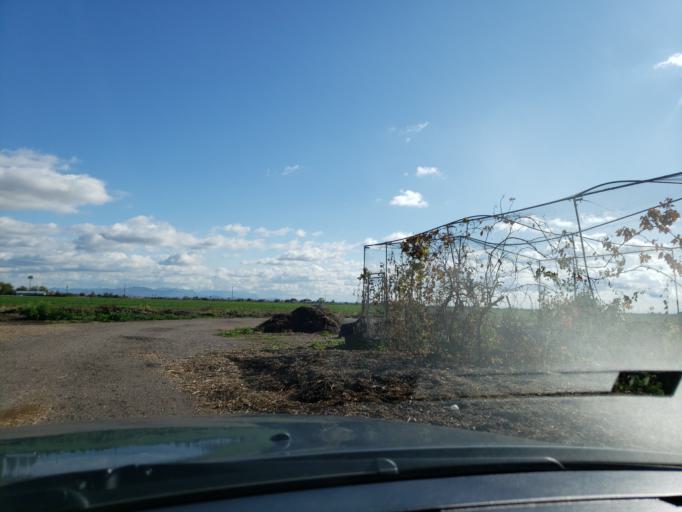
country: US
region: Arizona
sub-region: Maricopa County
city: Scottsdale
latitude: 33.5161
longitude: -111.8788
